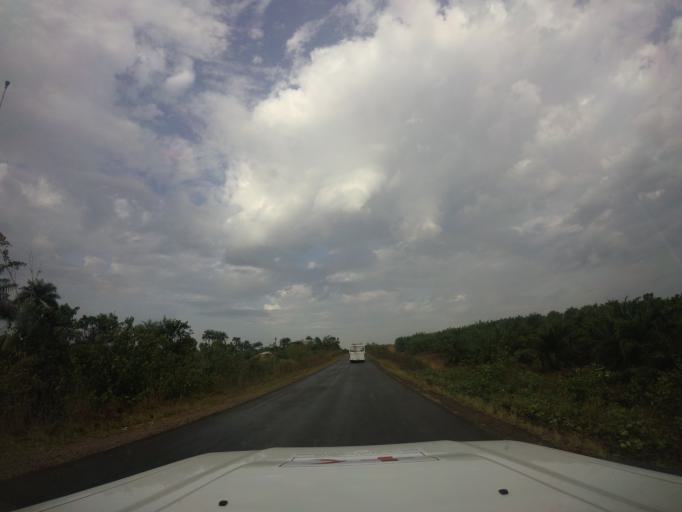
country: LR
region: Bomi
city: Tubmanburg
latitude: 6.7315
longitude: -11.0016
